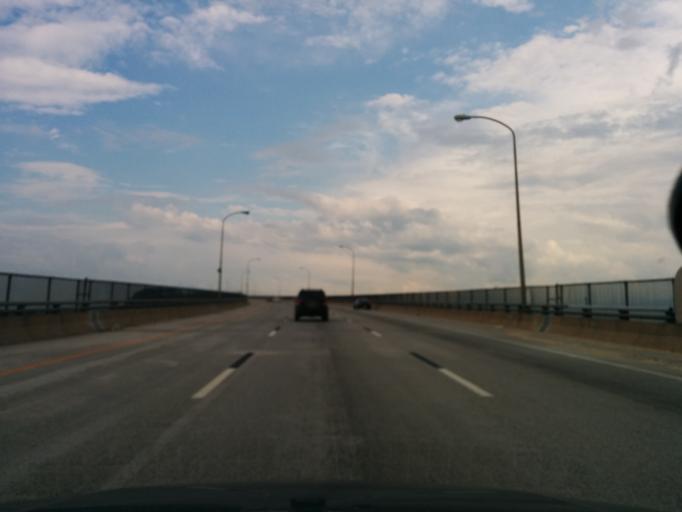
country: US
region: New Jersey
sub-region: Gloucester County
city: National Park
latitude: 39.8968
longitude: -75.1899
